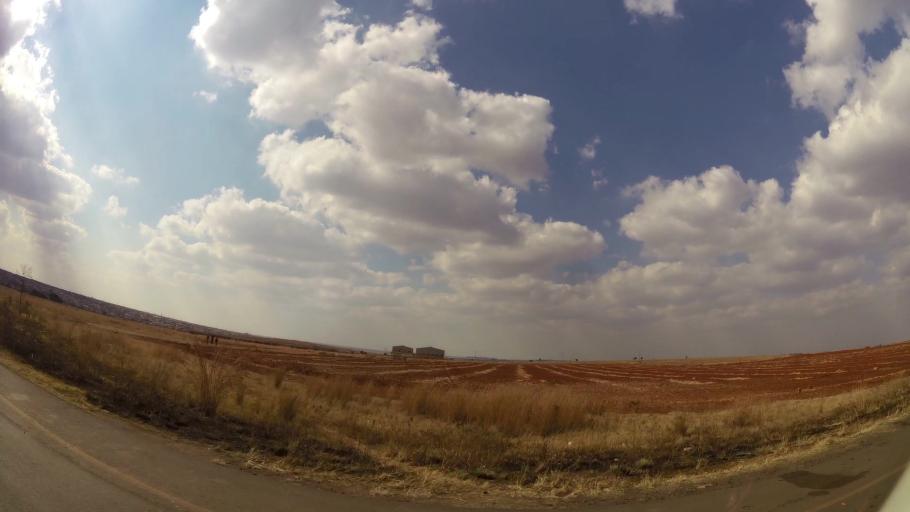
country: ZA
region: Mpumalanga
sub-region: Nkangala District Municipality
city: Delmas
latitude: -26.1148
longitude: 28.6802
